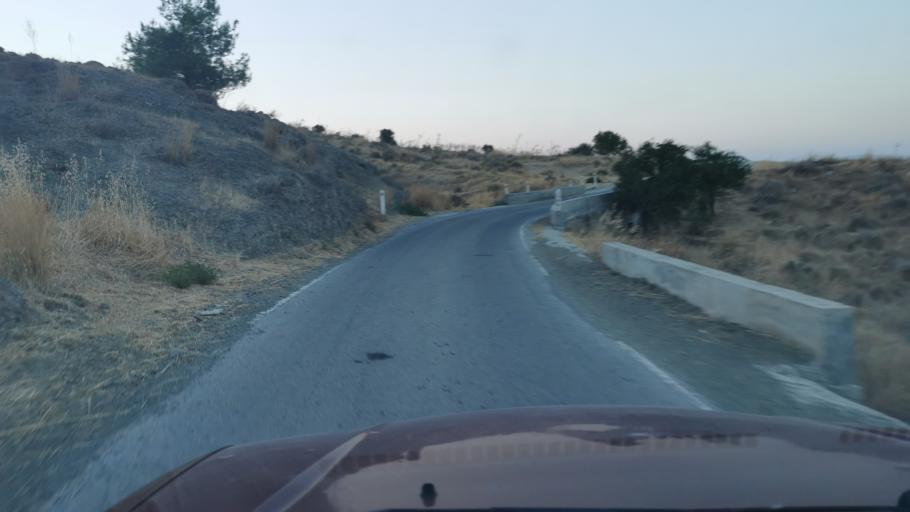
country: CY
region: Lefkosia
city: Peristerona
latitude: 35.0648
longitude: 33.0789
